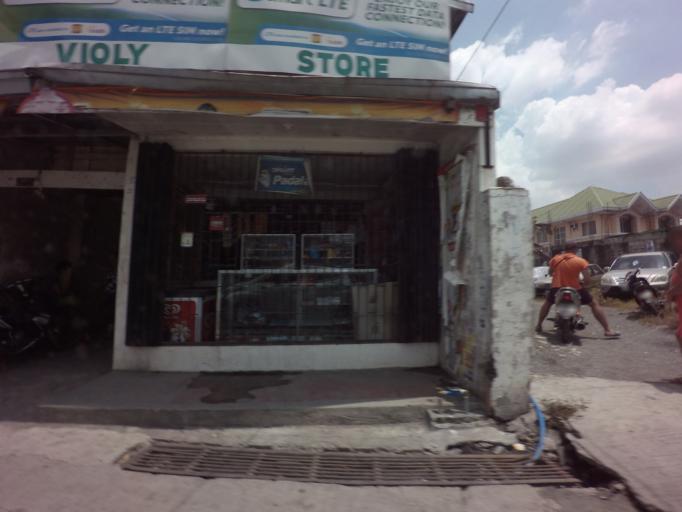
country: PH
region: Calabarzon
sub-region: Province of Laguna
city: San Pedro
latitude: 14.3832
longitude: 121.0514
